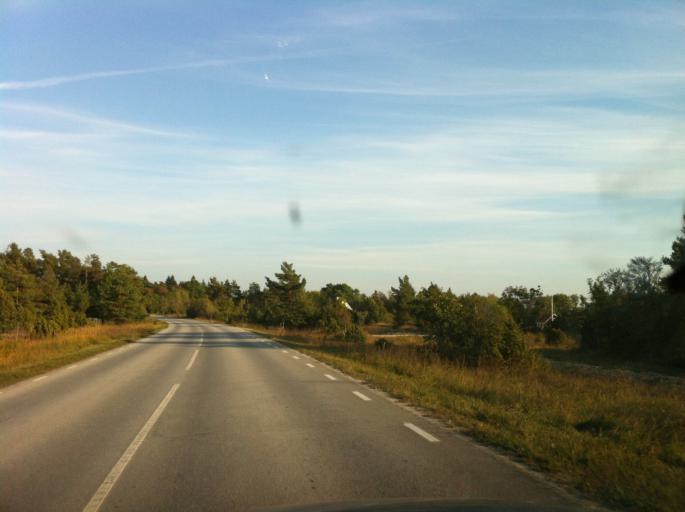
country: SE
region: Gotland
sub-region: Gotland
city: Slite
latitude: 57.4281
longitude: 18.7630
